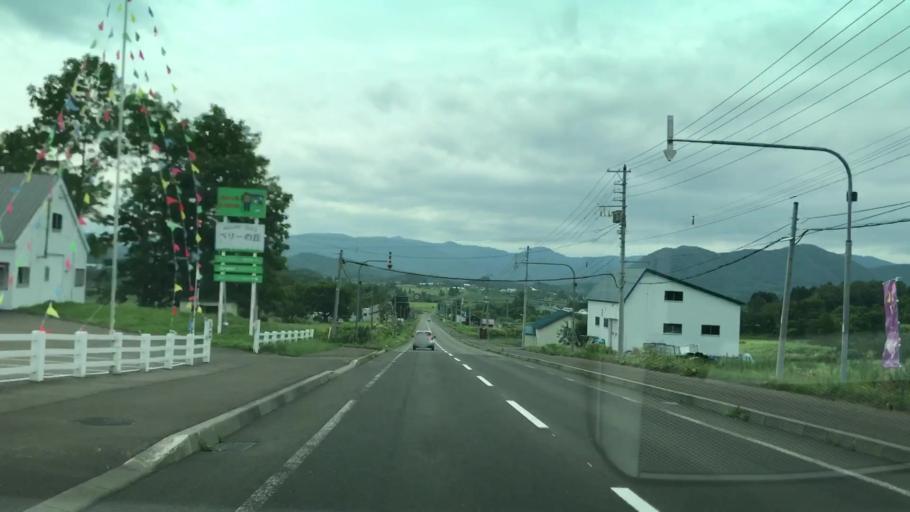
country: JP
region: Hokkaido
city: Yoichi
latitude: 43.1063
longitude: 140.8234
